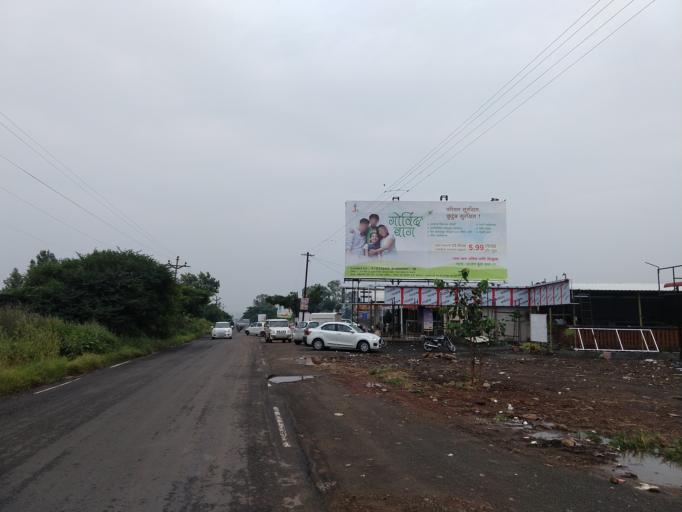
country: IN
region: Maharashtra
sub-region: Pune Division
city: Khed
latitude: 18.4027
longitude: 73.9117
